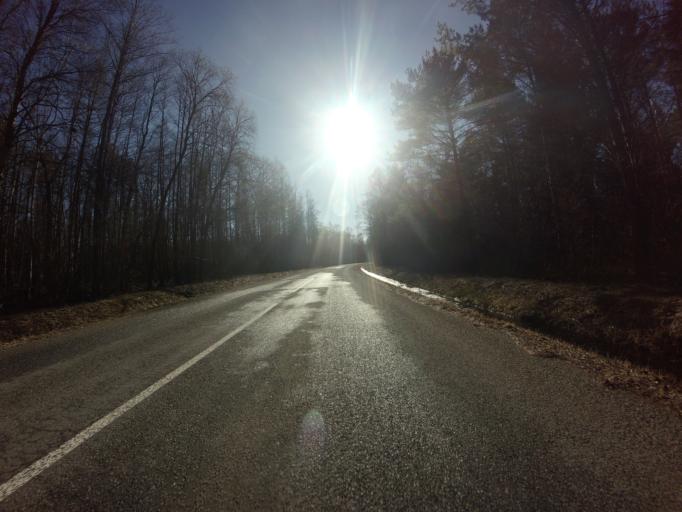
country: EE
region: Saare
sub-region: Kuressaare linn
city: Kuressaare
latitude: 58.4874
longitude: 22.3002
